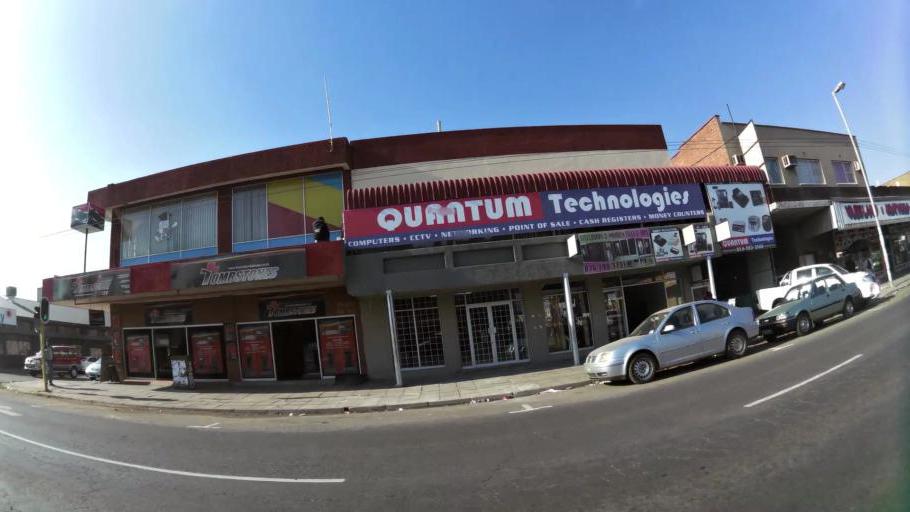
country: ZA
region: North-West
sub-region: Bojanala Platinum District Municipality
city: Rustenburg
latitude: -25.6706
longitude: 27.2411
